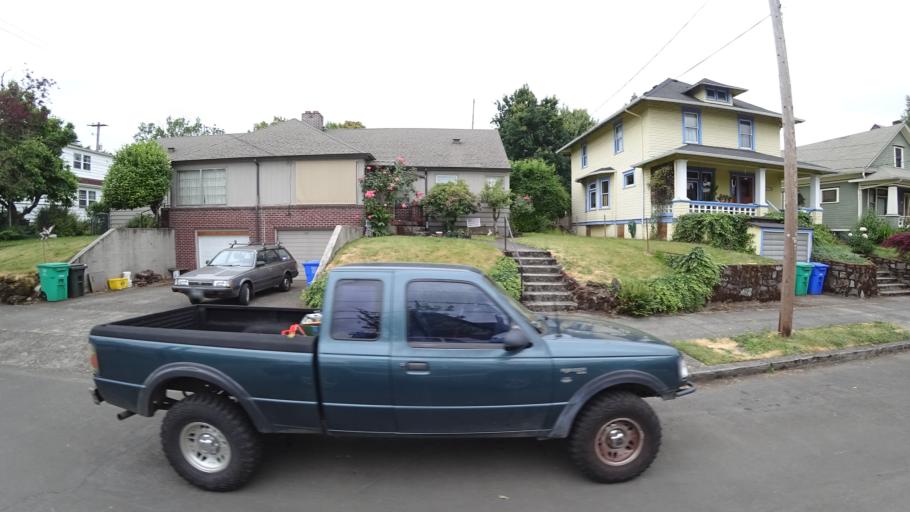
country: US
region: Oregon
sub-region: Multnomah County
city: Portland
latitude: 45.4969
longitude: -122.6579
